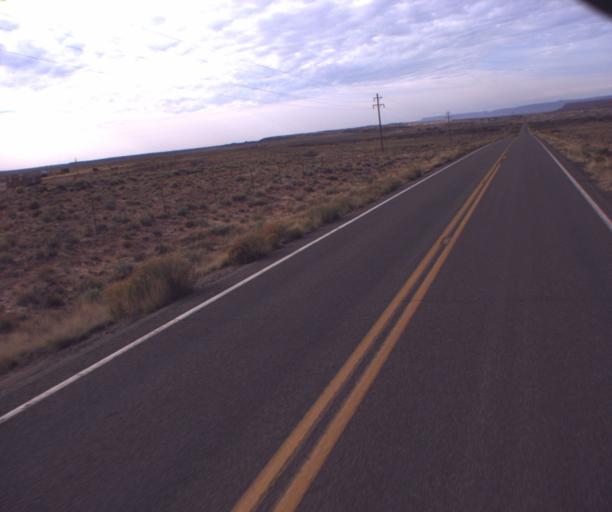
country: US
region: Arizona
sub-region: Apache County
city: Many Farms
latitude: 36.5023
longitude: -109.4812
